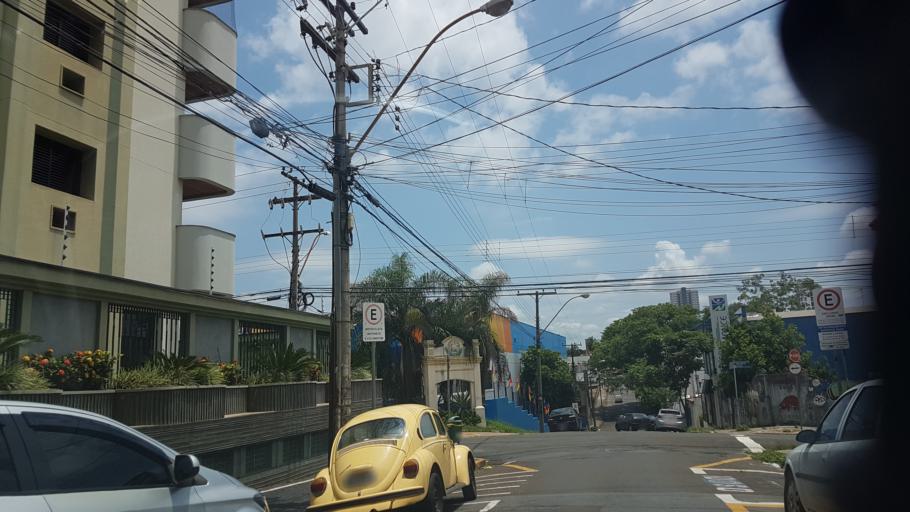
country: BR
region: Sao Paulo
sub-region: Piracicaba
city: Piracicaba
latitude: -22.7218
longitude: -47.6460
